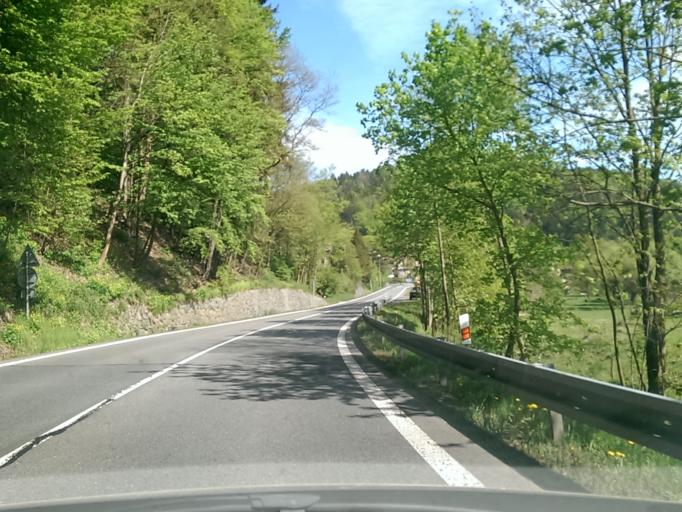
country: CZ
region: Liberecky
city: Mala Skala
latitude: 50.6549
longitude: 15.2156
